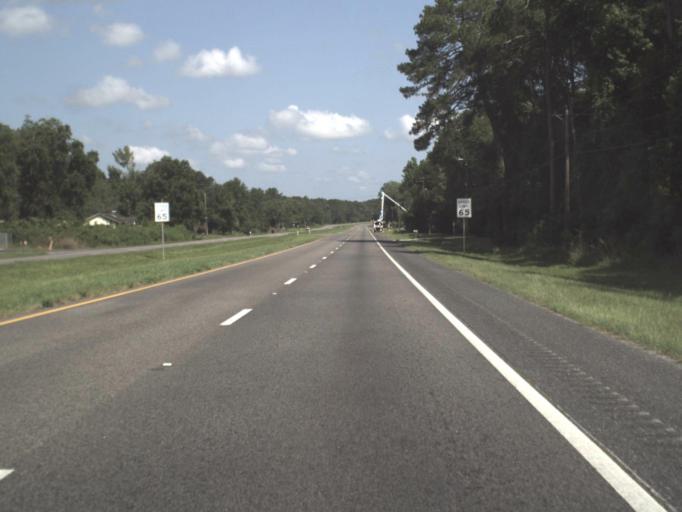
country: US
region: Florida
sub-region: Alachua County
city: Gainesville
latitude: 29.5429
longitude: -82.3174
